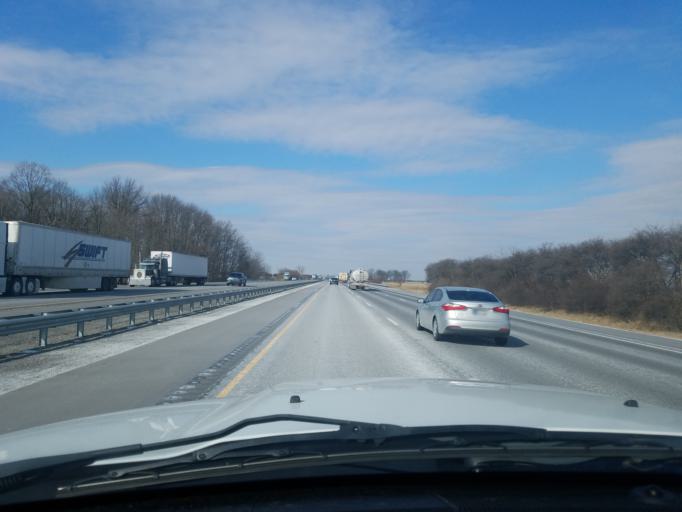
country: US
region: Indiana
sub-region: Johnson County
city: Franklin
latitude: 39.5092
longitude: -86.0211
